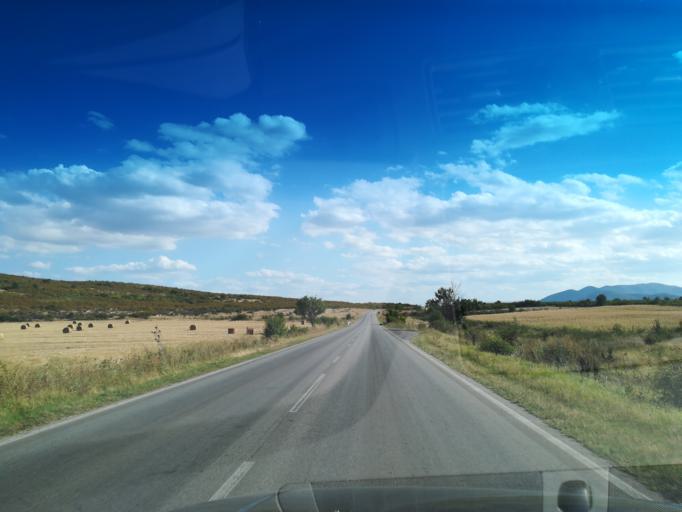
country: BG
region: Khaskovo
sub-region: Obshtina Mineralni Bani
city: Mineralni Bani
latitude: 41.9798
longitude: 25.3528
